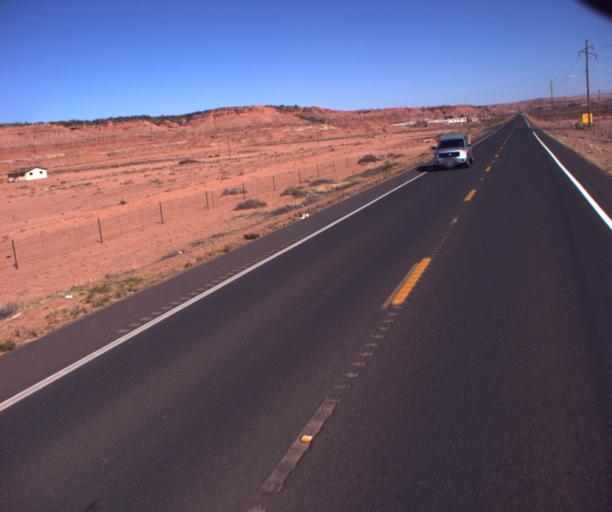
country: US
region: Arizona
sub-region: Coconino County
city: Tuba City
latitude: 36.1039
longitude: -111.2786
